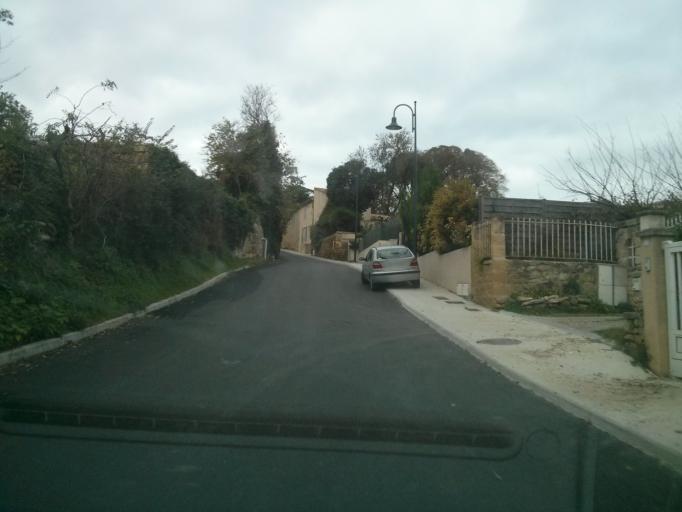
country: FR
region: Languedoc-Roussillon
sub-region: Departement du Gard
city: Aigues-Vives
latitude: 43.7378
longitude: 4.1843
